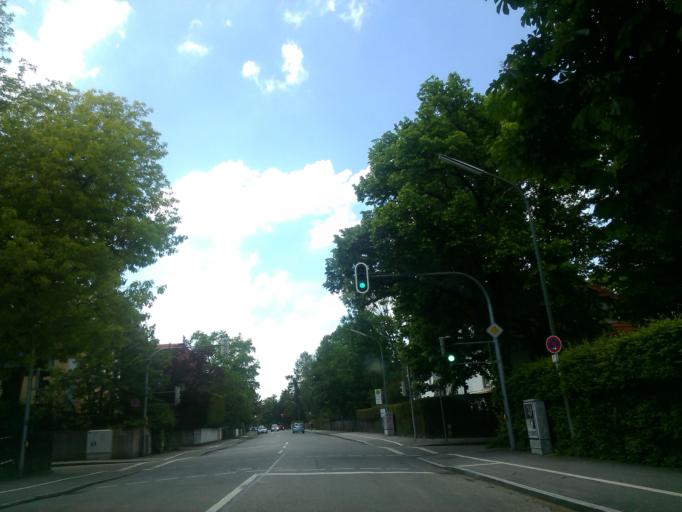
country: DE
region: Bavaria
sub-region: Upper Bavaria
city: Pullach im Isartal
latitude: 48.0824
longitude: 11.5202
